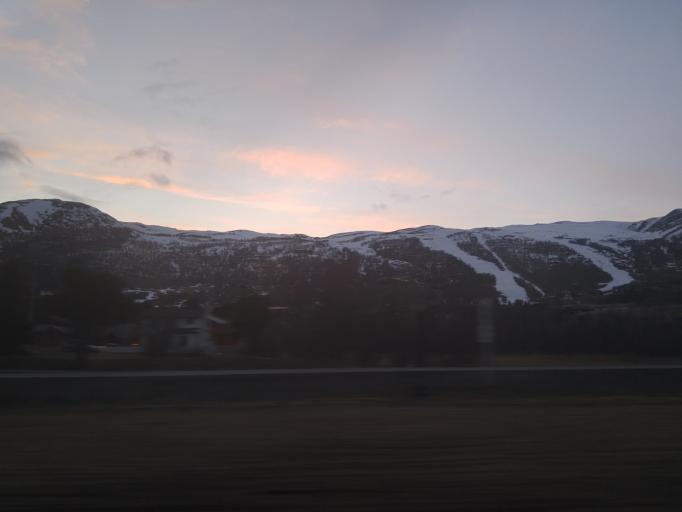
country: NO
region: Sor-Trondelag
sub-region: Oppdal
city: Oppdal
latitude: 62.6057
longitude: 9.7346
